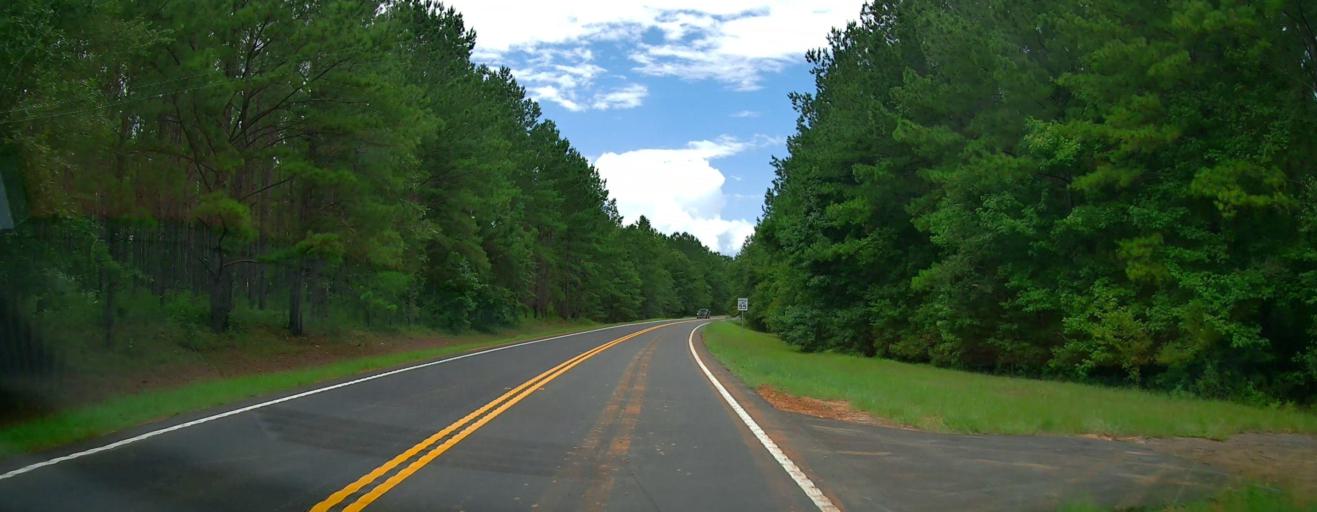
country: US
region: Georgia
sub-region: Dooly County
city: Vienna
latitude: 32.0803
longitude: -83.6092
